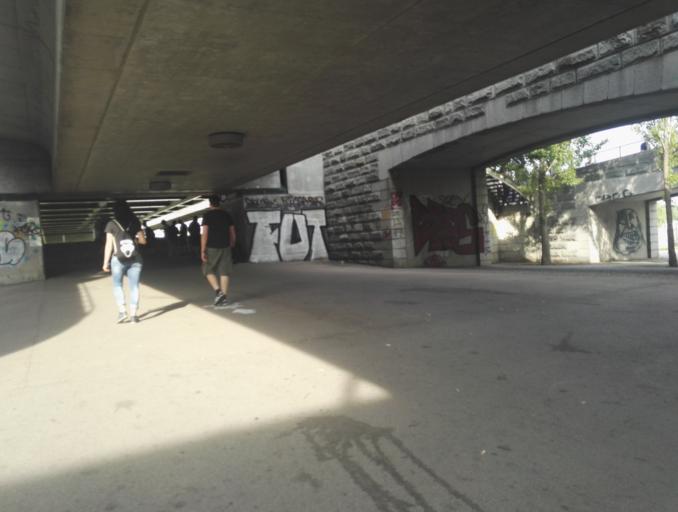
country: AT
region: Vienna
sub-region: Wien Stadt
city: Vienna
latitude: 48.2422
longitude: 16.3863
